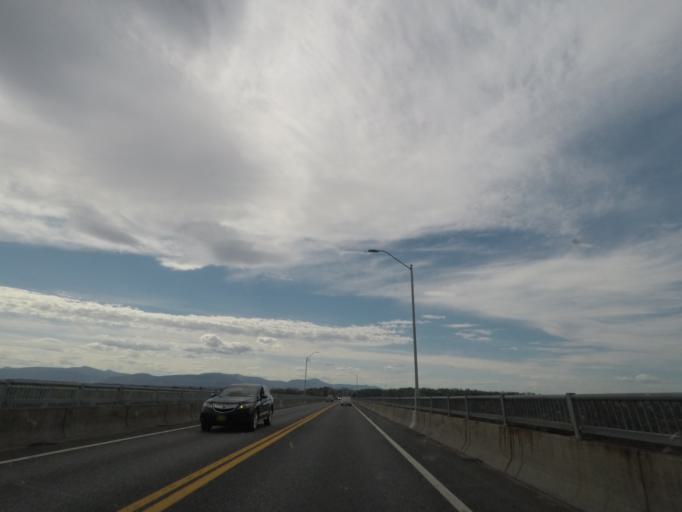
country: US
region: New York
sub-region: Greene County
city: Catskill
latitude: 42.2210
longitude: -73.8404
